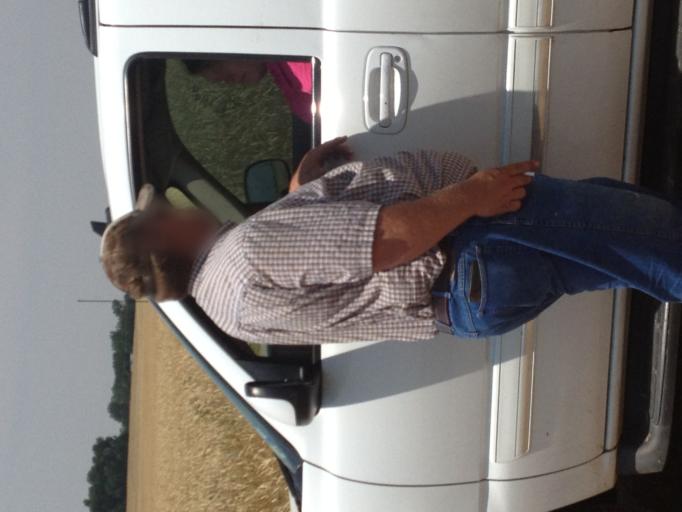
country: US
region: Kansas
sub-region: Barton County
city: Ellinwood
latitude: 38.2430
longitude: -98.5550
